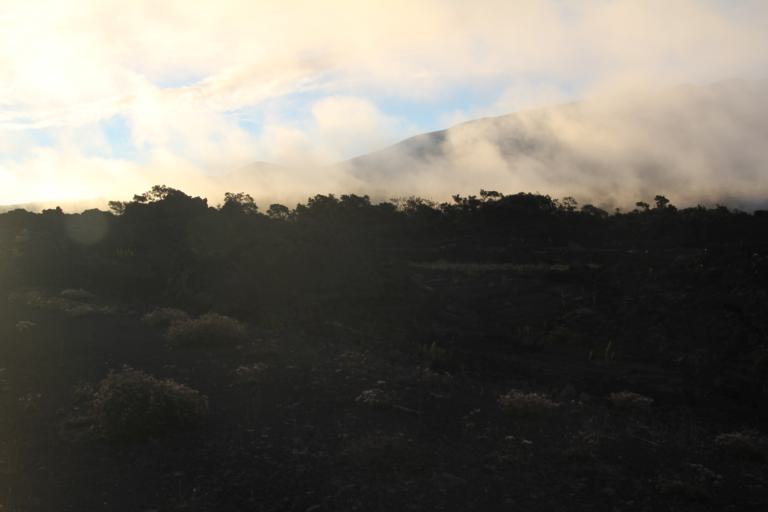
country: US
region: Hawaii
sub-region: Hawaii County
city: Volcano
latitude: 19.6833
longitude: -155.4109
